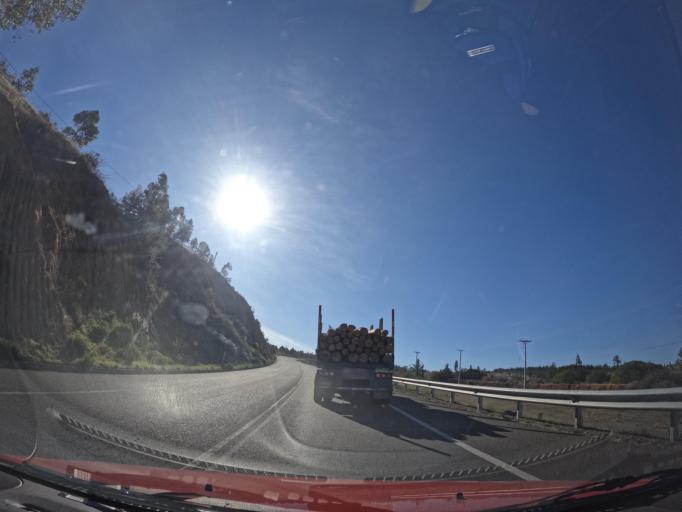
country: CL
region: Maule
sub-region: Provincia de Cauquenes
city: Cauquenes
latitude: -35.9377
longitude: -72.1955
